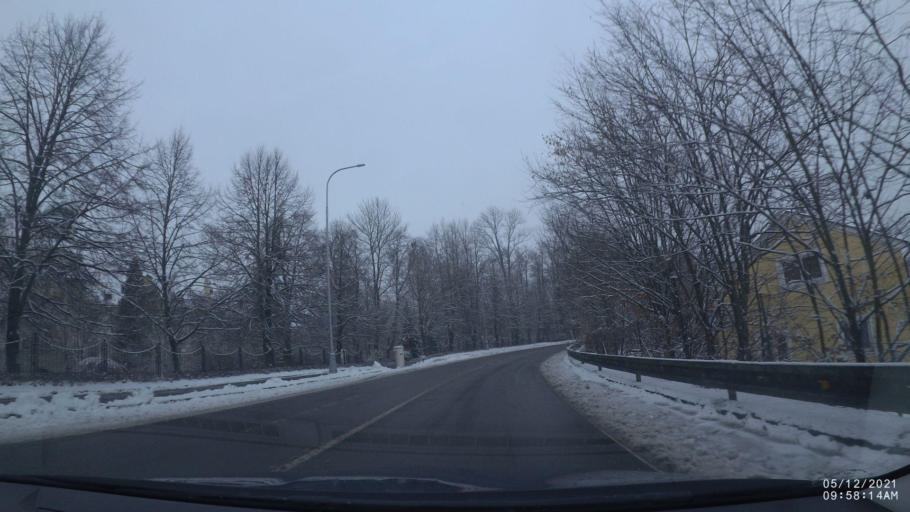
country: CZ
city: Castolovice
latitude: 50.1302
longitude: 16.1861
